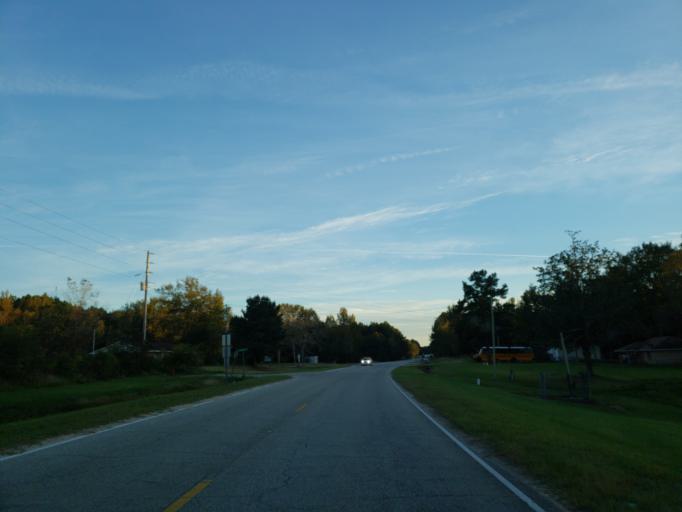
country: US
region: Mississippi
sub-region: Wayne County
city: Belmont
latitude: 31.4223
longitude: -88.4708
